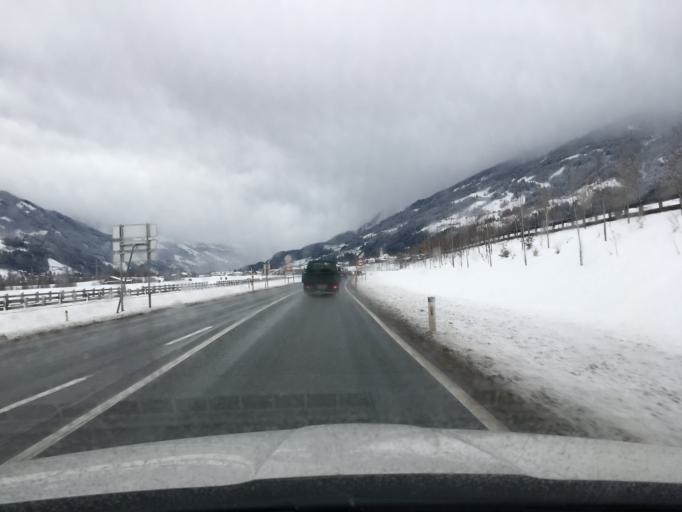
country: AT
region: Tyrol
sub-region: Politischer Bezirk Schwaz
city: Uderns
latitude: 47.3157
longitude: 11.8660
